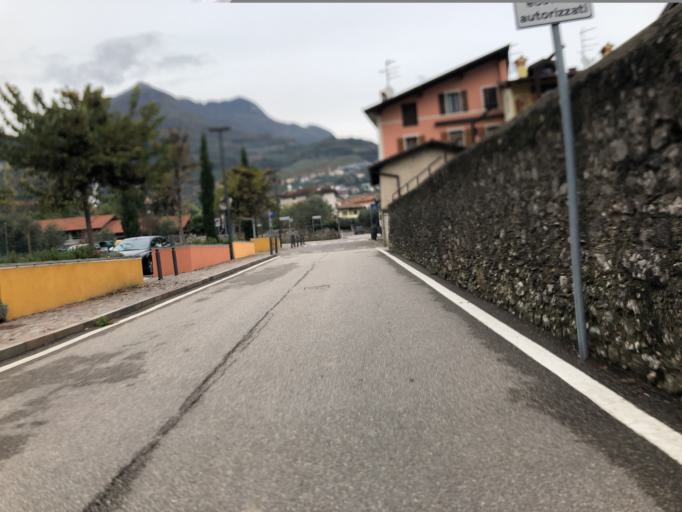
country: IT
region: Trentino-Alto Adige
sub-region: Provincia di Trento
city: Tenno
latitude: 45.9044
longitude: 10.8400
